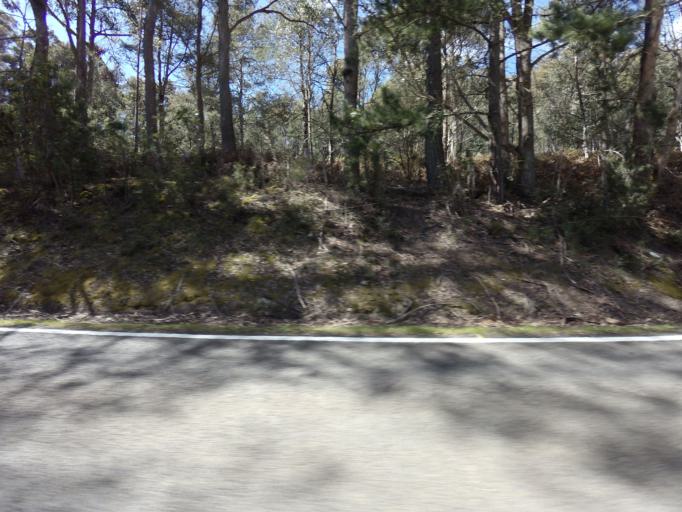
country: AU
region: Tasmania
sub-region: Derwent Valley
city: New Norfolk
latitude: -42.6987
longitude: 146.7136
